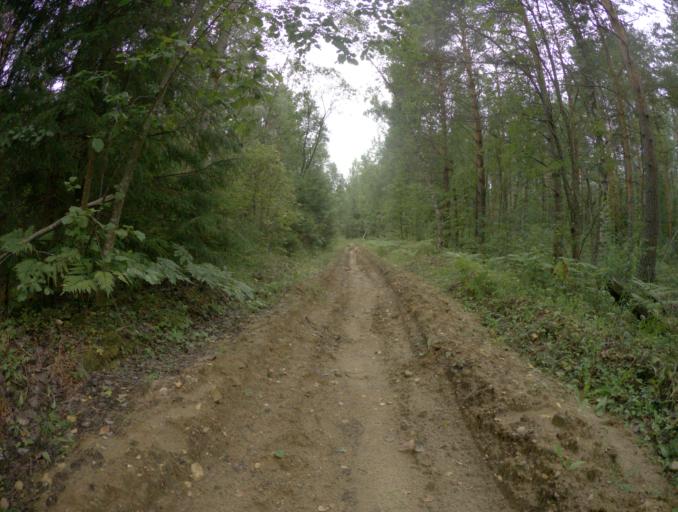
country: RU
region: Vladimir
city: Raduzhnyy
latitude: 55.9821
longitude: 40.2661
